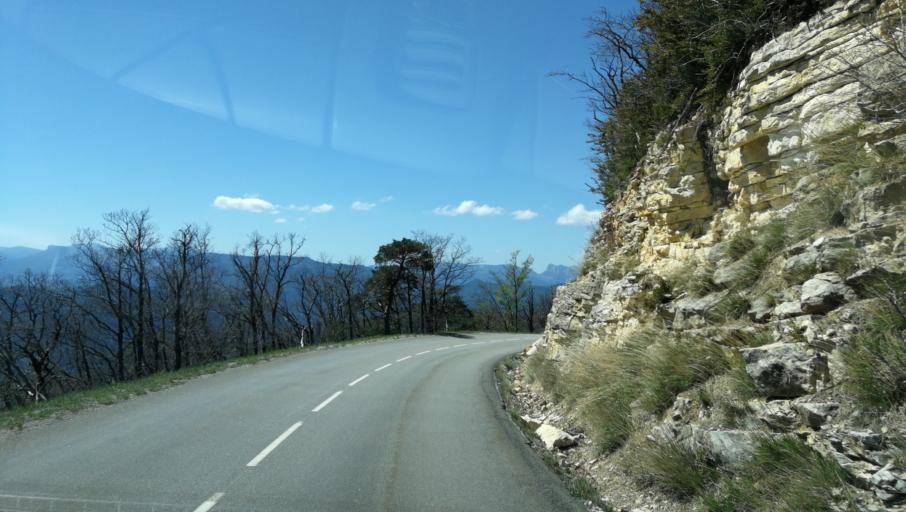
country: FR
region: Rhone-Alpes
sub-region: Departement de la Drome
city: Die
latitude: 44.8273
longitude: 5.3899
